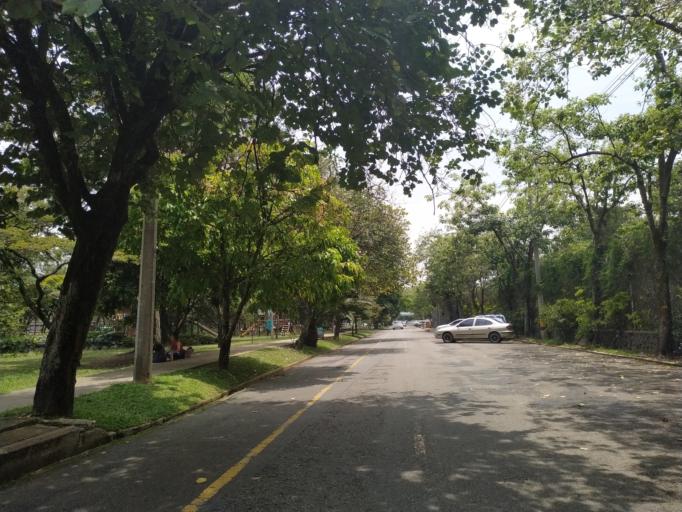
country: CO
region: Antioquia
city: Medellin
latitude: 6.2692
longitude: -75.5704
